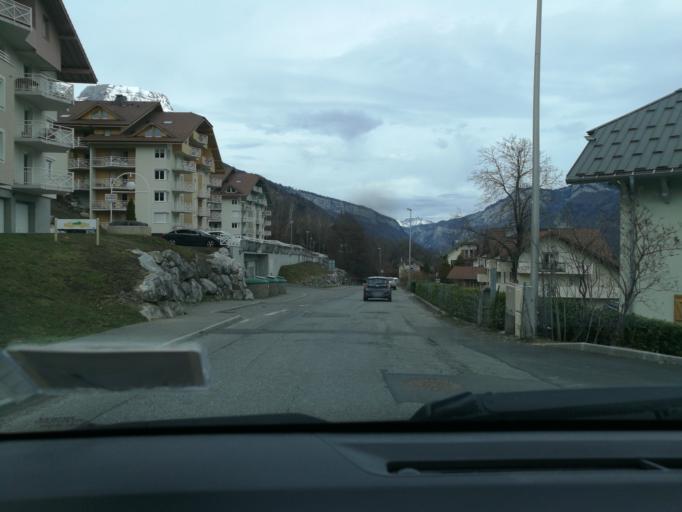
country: FR
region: Rhone-Alpes
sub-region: Departement de la Haute-Savoie
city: Sallanches
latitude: 45.9311
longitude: 6.6297
